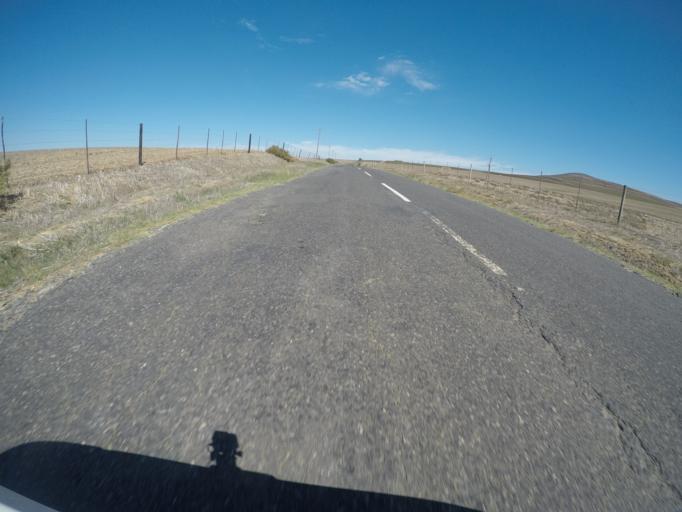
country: ZA
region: Western Cape
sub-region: City of Cape Town
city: Atlantis
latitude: -33.7033
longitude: 18.5869
